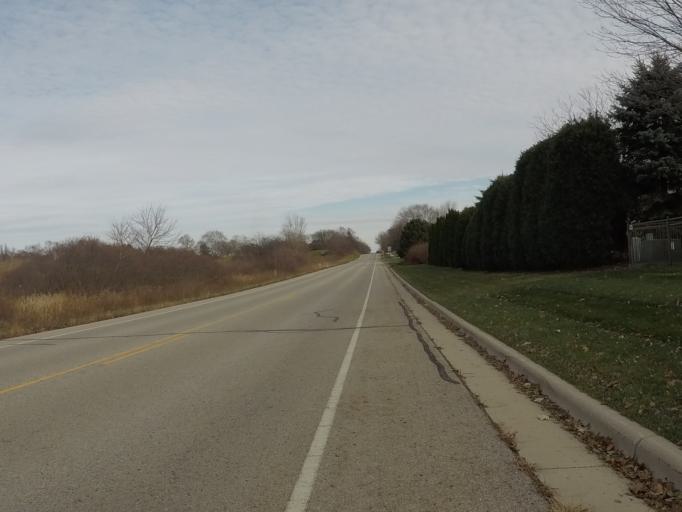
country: US
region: Wisconsin
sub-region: Dane County
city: Middleton
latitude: 43.0820
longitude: -89.5486
